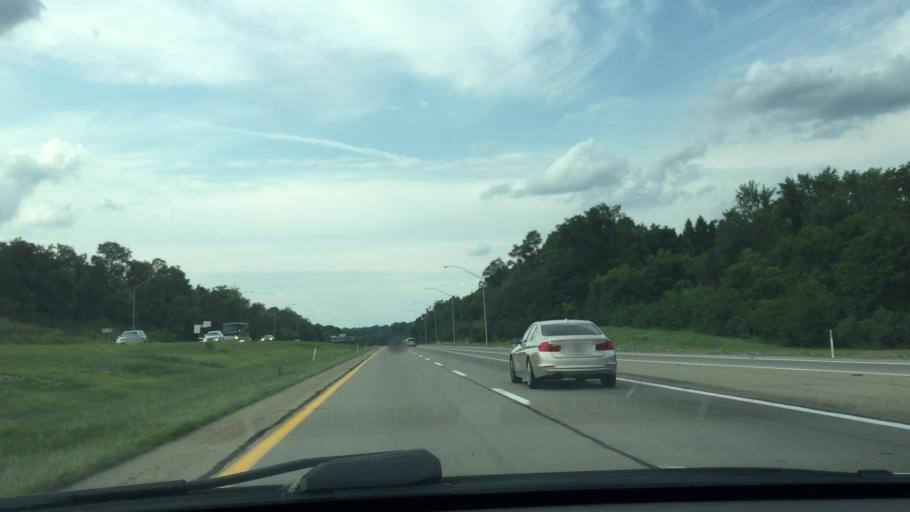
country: US
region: Pennsylvania
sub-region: Allegheny County
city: Ingram
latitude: 40.4524
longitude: -80.1110
